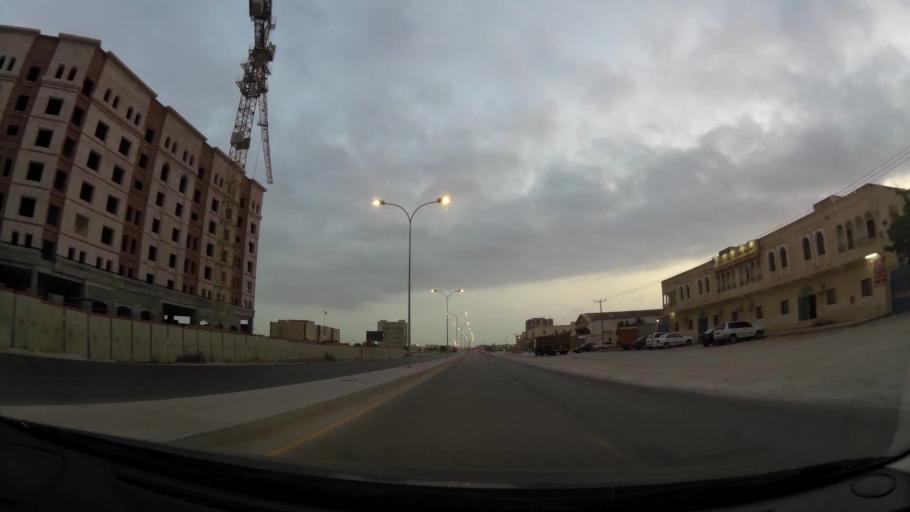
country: OM
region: Zufar
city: Salalah
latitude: 17.0231
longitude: 54.0389
